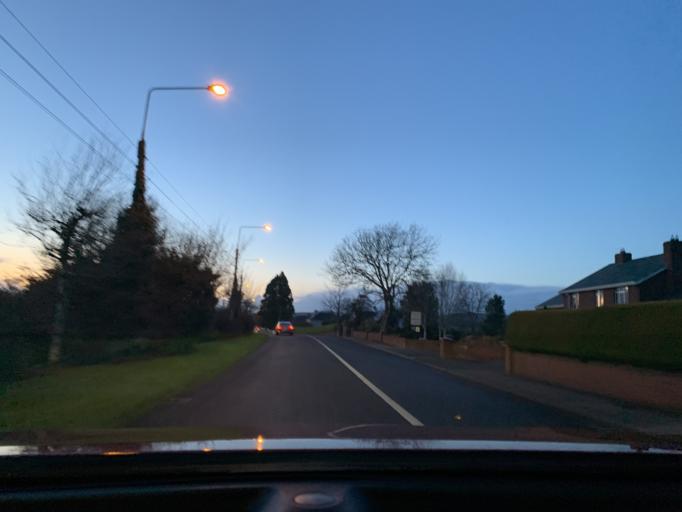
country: IE
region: Connaught
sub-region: Roscommon
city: Boyle
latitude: 53.9708
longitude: -8.2845
